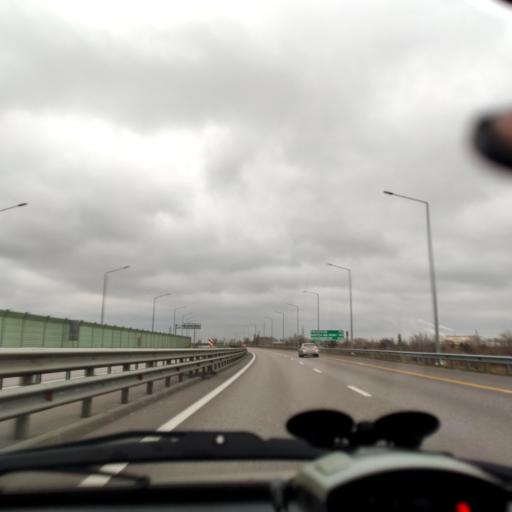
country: RU
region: Voronezj
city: Novaya Usman'
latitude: 51.6351
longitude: 39.3170
